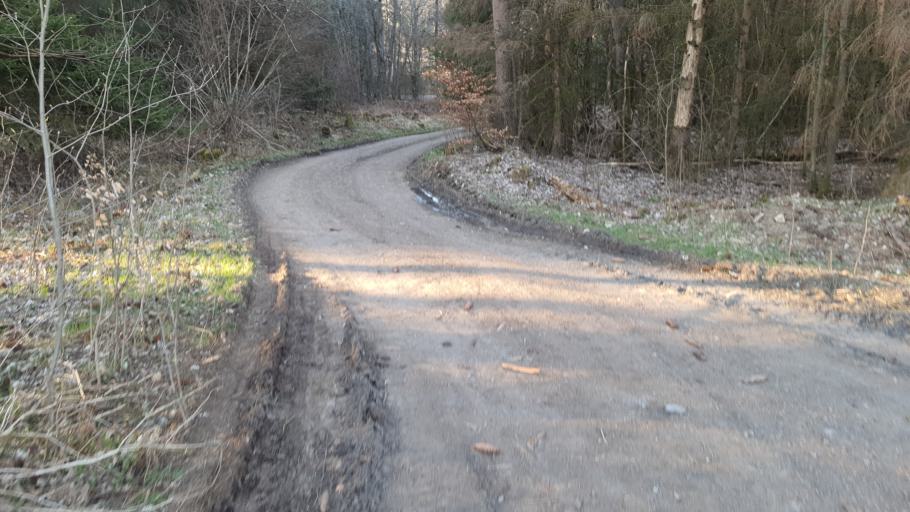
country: DE
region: Hesse
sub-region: Regierungsbezirk Giessen
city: Greifenstein
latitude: 50.6258
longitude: 8.2717
